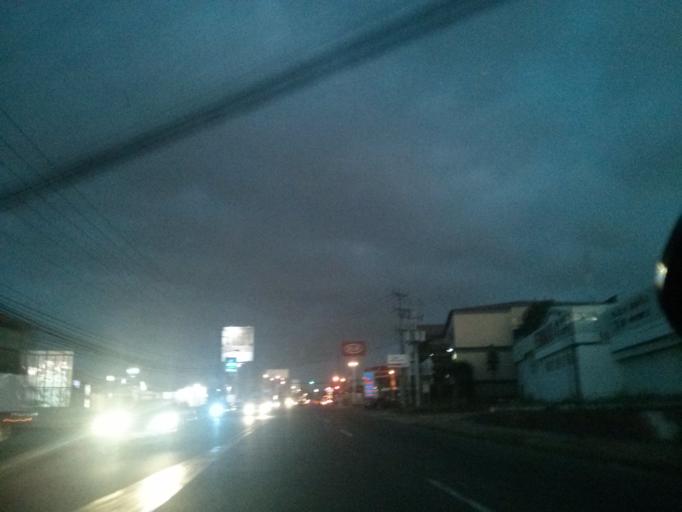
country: CR
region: San Jose
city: Colima
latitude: 9.9515
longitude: -84.1053
